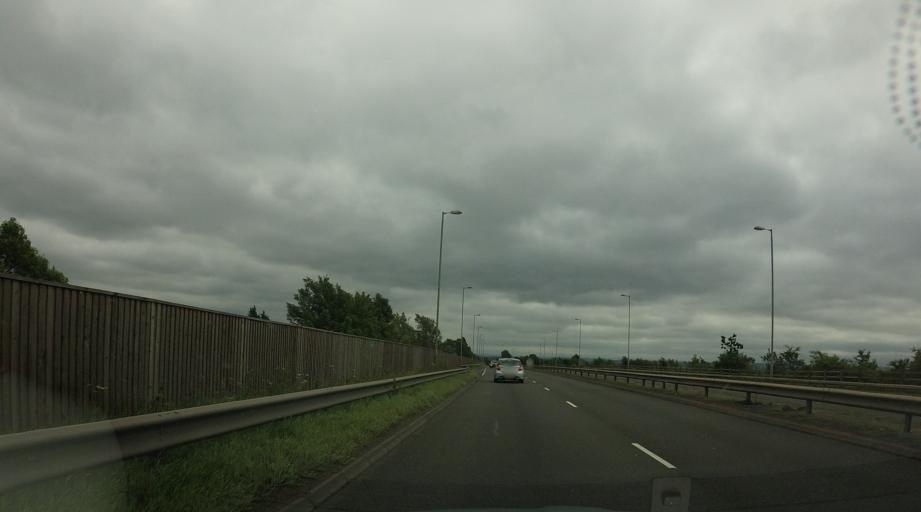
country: GB
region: Scotland
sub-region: North Lanarkshire
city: Bellshill
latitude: 55.8153
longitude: -4.0387
